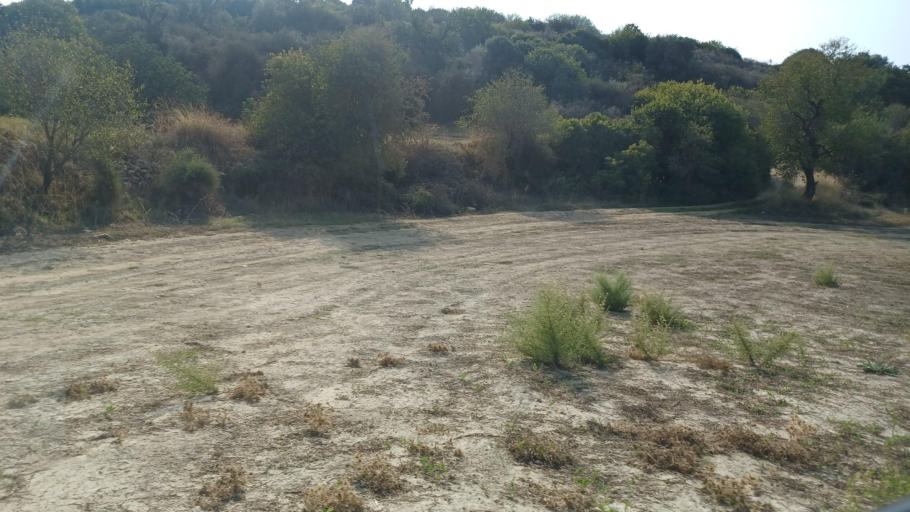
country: CY
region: Pafos
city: Polis
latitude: 34.9766
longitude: 32.4555
